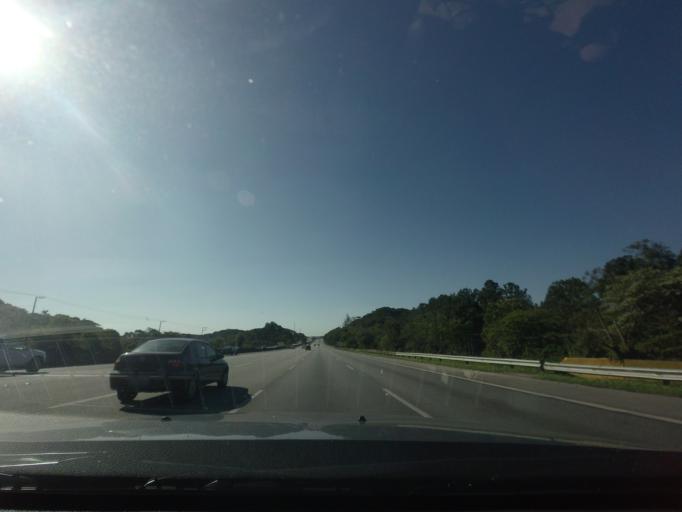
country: BR
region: Sao Paulo
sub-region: Sao Bernardo Do Campo
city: Sao Bernardo do Campo
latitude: -23.8323
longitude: -46.5793
